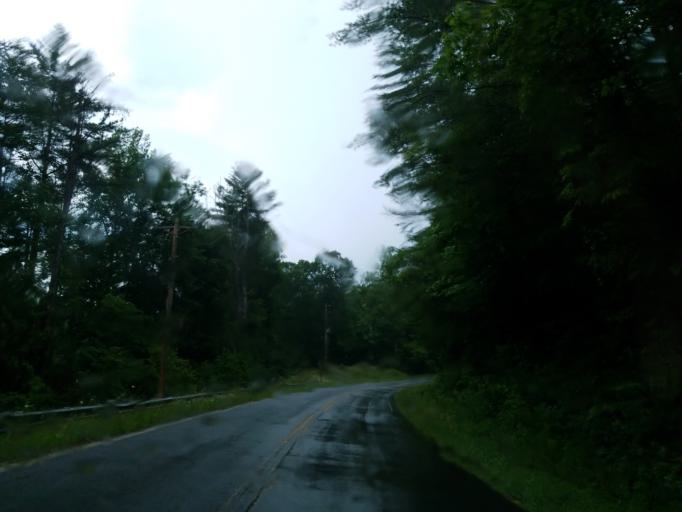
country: US
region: Georgia
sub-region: Fannin County
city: Blue Ridge
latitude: 34.7869
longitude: -84.2559
